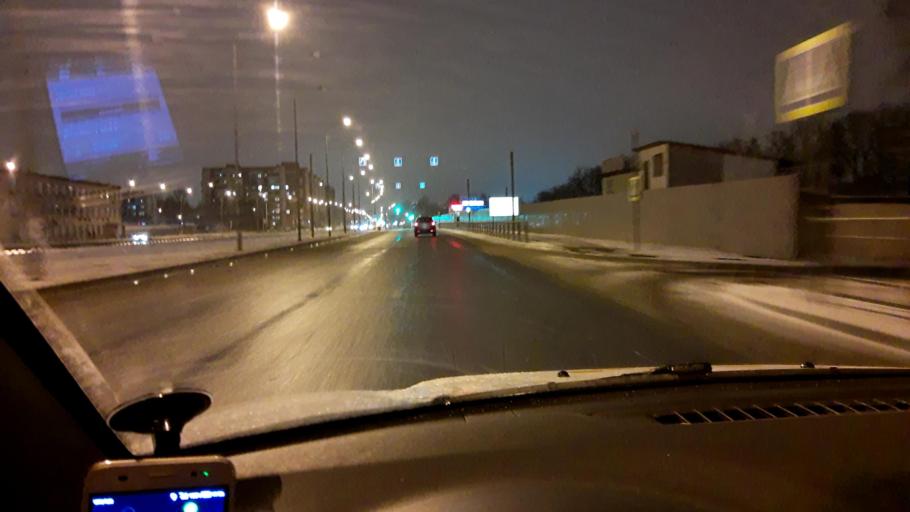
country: RU
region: Nizjnij Novgorod
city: Gorbatovka
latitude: 56.2455
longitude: 43.8187
